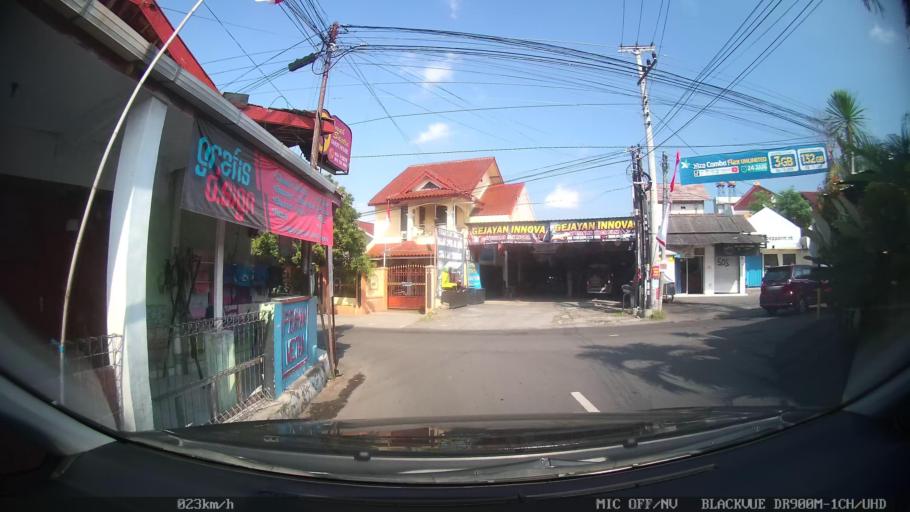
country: ID
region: Daerah Istimewa Yogyakarta
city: Depok
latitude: -7.7653
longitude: 110.3966
